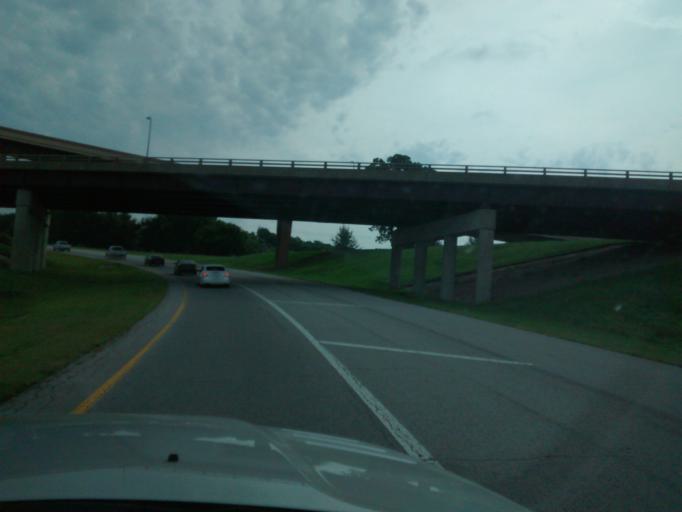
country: US
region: Arkansas
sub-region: Washington County
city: Johnson
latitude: 36.1170
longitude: -94.1463
